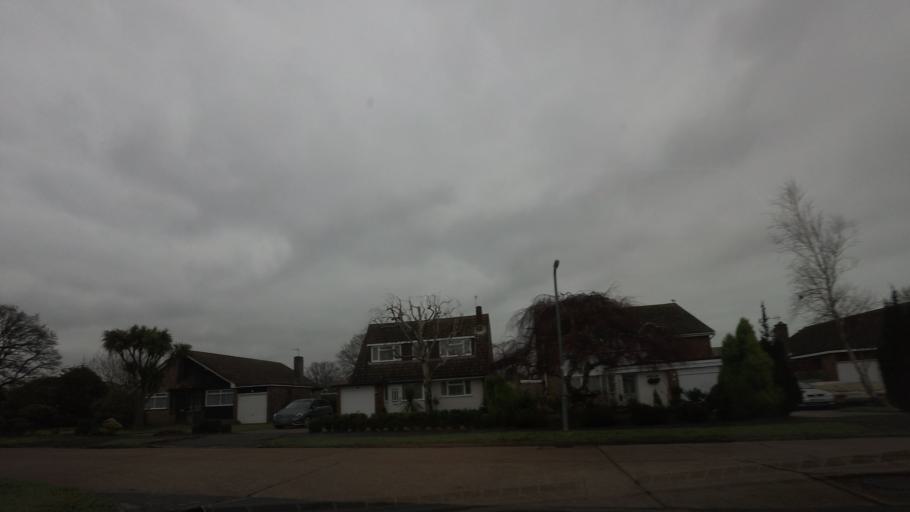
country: GB
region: England
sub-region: East Sussex
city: Bexhill-on-Sea
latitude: 50.8401
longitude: 0.4451
